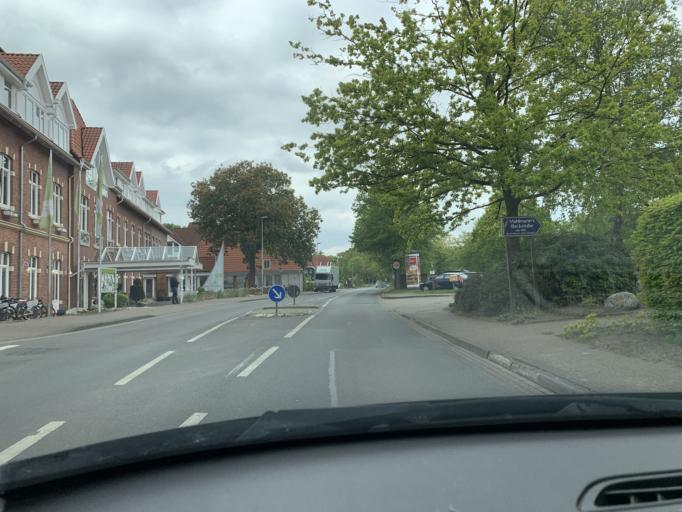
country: DE
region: Lower Saxony
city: Bad Zwischenahn
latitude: 53.2142
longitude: 8.0211
